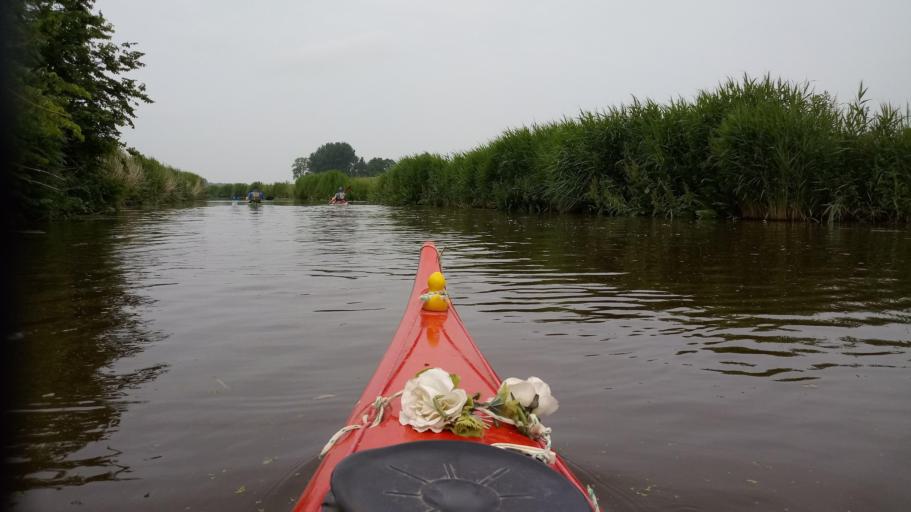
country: NL
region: Groningen
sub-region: Gemeente Winsum
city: Winsum
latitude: 53.3623
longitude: 6.5349
